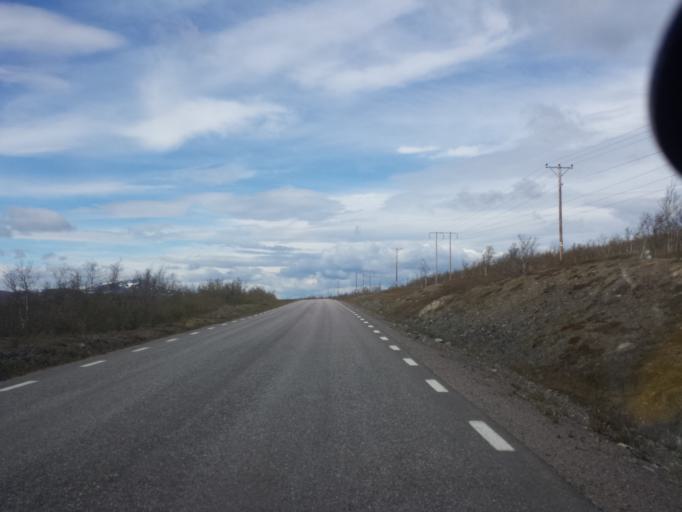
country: SE
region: Norrbotten
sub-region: Kiruna Kommun
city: Kiruna
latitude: 68.0461
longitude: 19.8304
